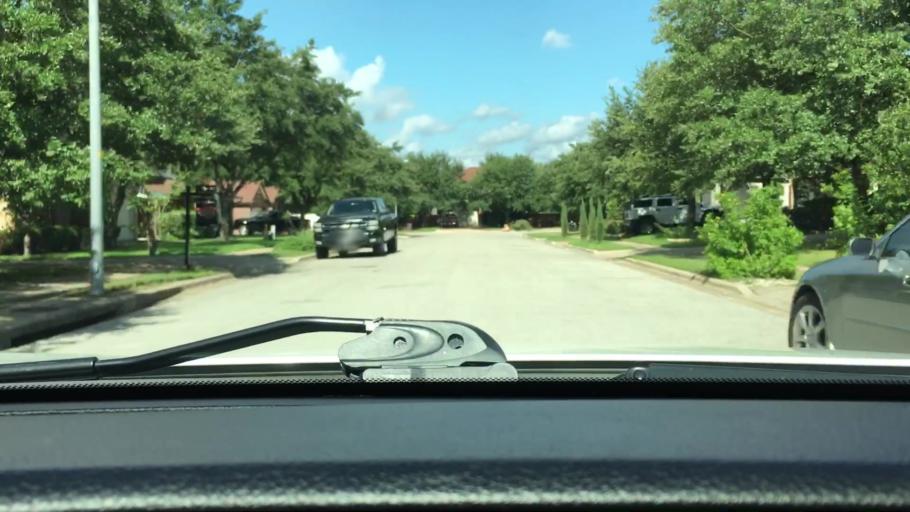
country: US
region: Texas
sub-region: Travis County
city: Windemere
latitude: 30.4768
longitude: -97.6466
